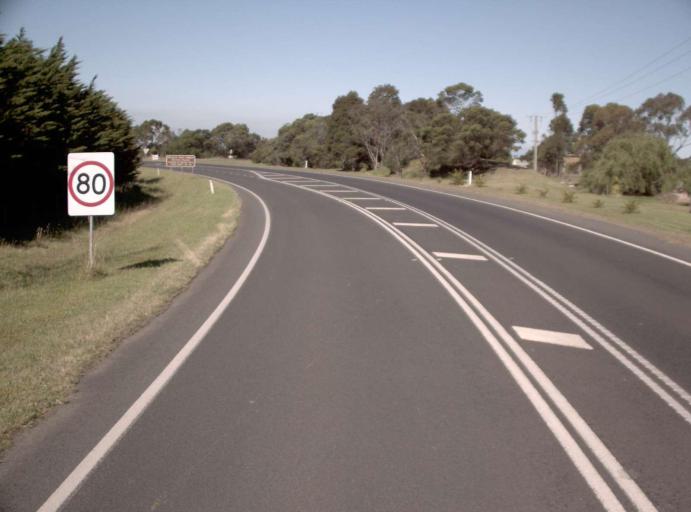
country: AU
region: Victoria
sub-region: Latrobe
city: Traralgon
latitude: -38.6219
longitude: 146.6661
